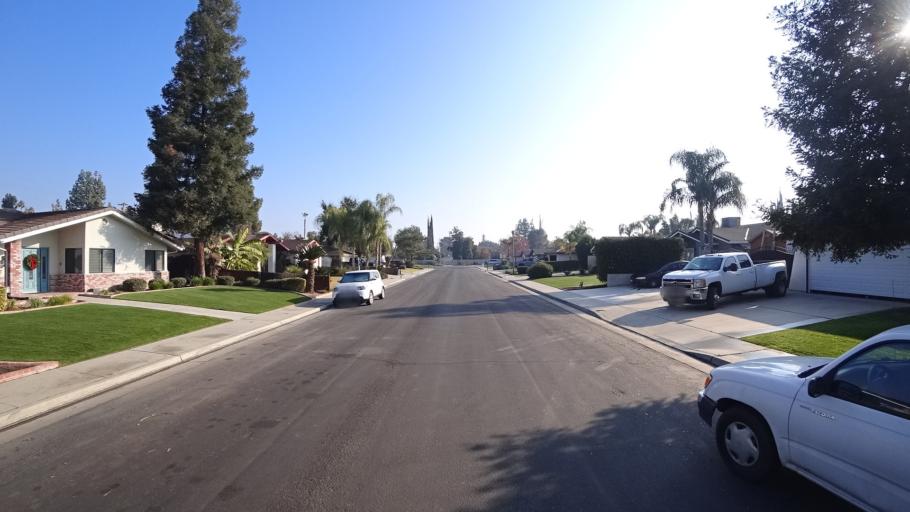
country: US
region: California
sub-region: Kern County
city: Greenacres
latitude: 35.3431
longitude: -119.0759
